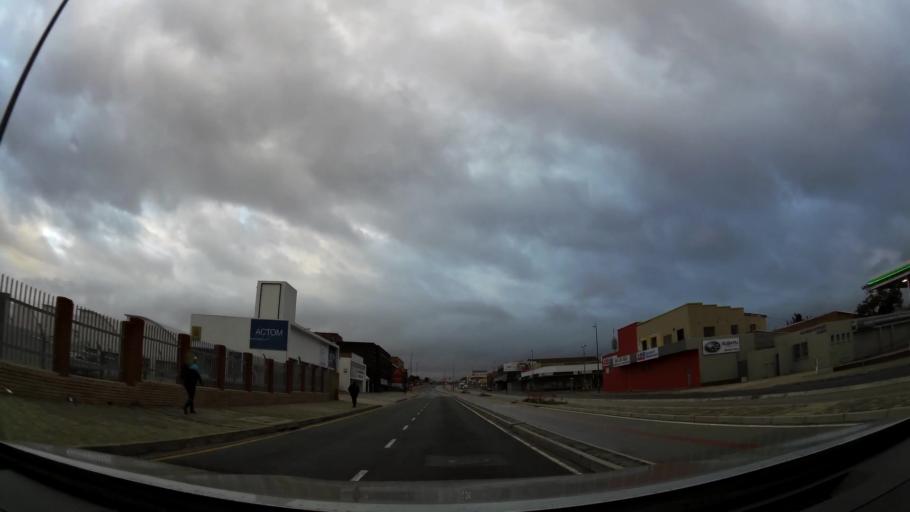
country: ZA
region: Eastern Cape
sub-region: Nelson Mandela Bay Metropolitan Municipality
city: Port Elizabeth
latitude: -33.9218
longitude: 25.5967
